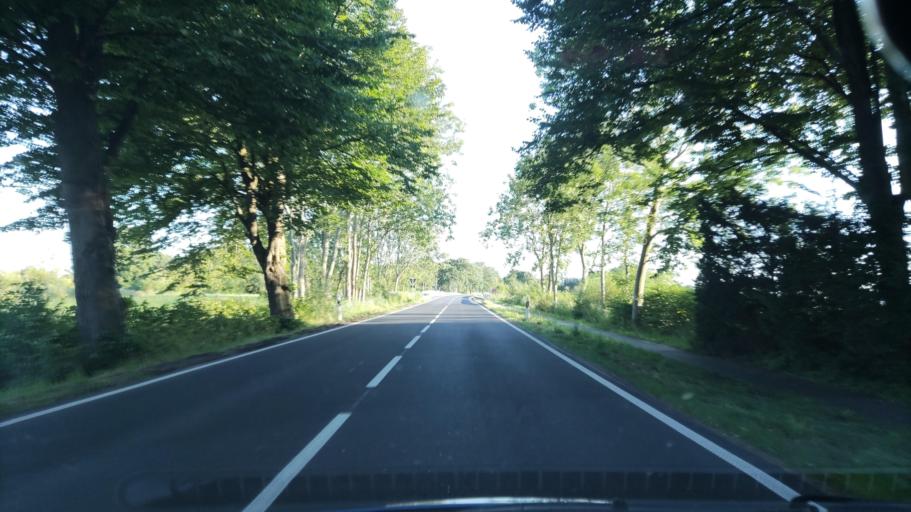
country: DE
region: Lower Saxony
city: Werdum
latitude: 53.6839
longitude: 7.7989
